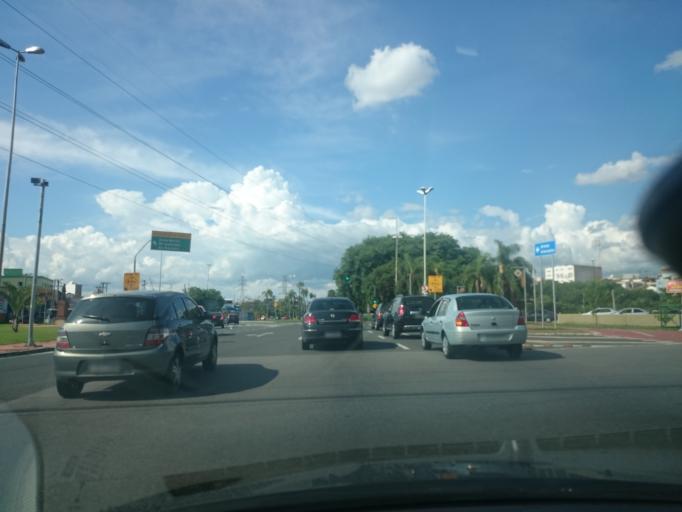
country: BR
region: Sao Paulo
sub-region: Sorocaba
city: Sorocaba
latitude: -23.5079
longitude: -47.4521
